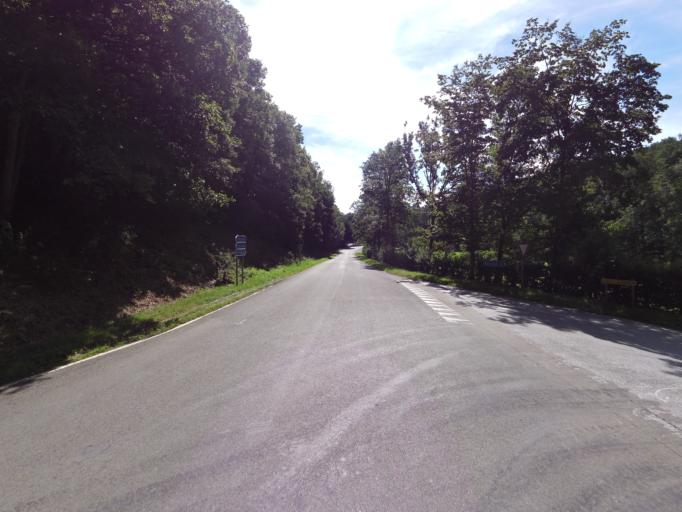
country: BE
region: Wallonia
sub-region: Province du Luxembourg
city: Nassogne
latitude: 50.0864
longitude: 5.3377
